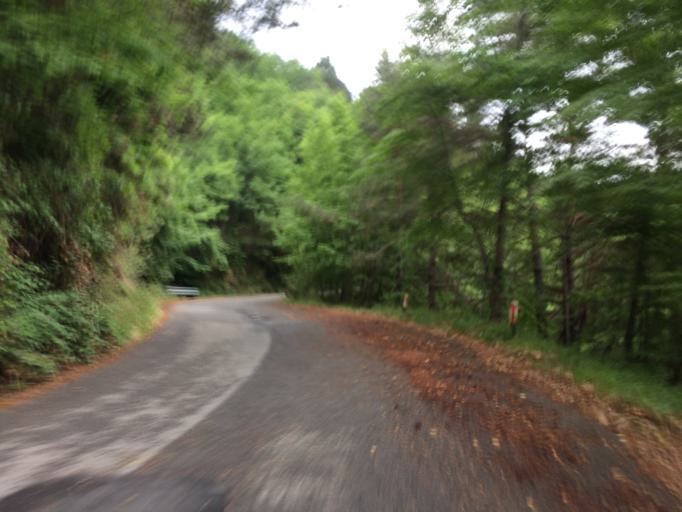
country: IT
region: Liguria
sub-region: Provincia di Imperia
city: Triora
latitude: 43.9738
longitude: 7.7446
